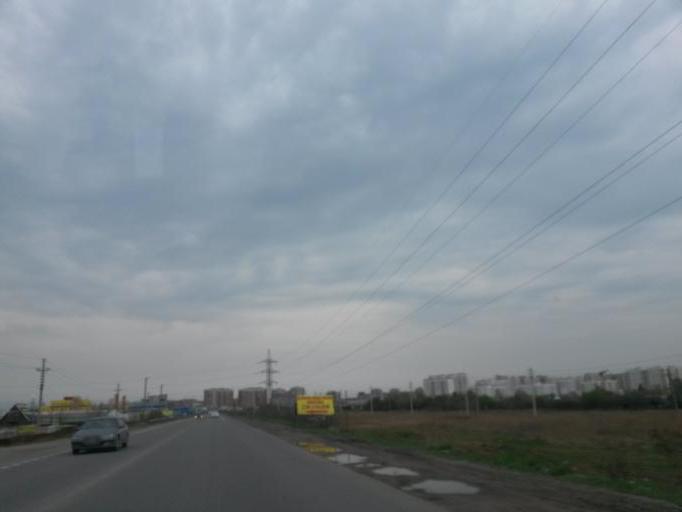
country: RU
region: Moskovskaya
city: Shcherbinka
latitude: 55.4937
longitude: 37.5841
